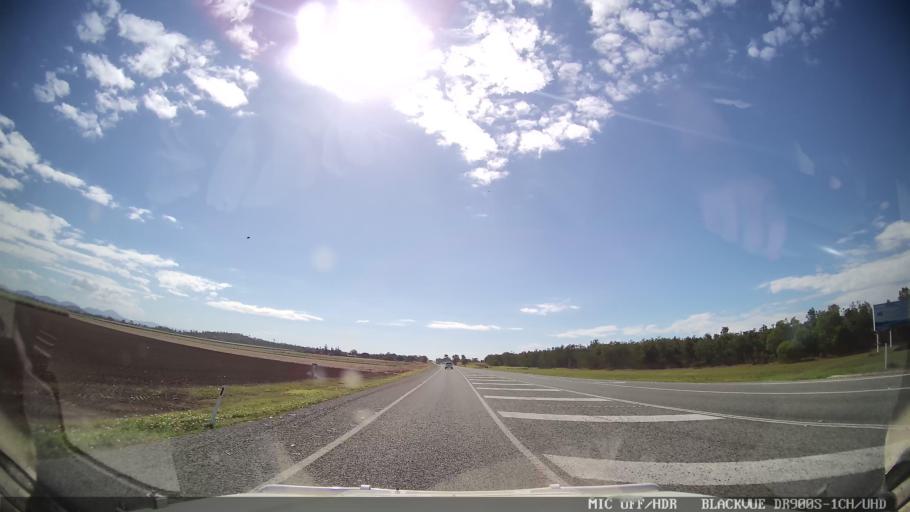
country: AU
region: Queensland
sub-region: Whitsunday
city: Proserpine
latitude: -20.5729
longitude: 148.6197
